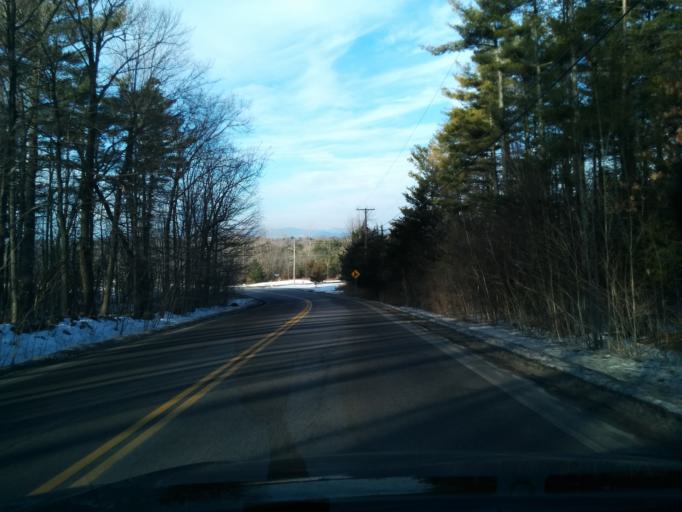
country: US
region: Vermont
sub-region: Chittenden County
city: South Burlington
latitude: 44.3727
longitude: -73.2099
